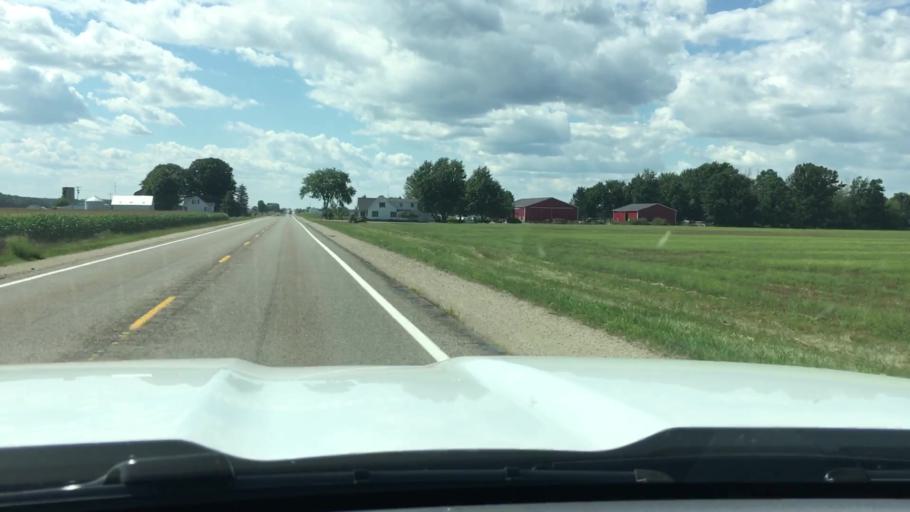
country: US
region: Michigan
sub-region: Gratiot County
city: Ithaca
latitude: 43.1757
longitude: -84.5345
